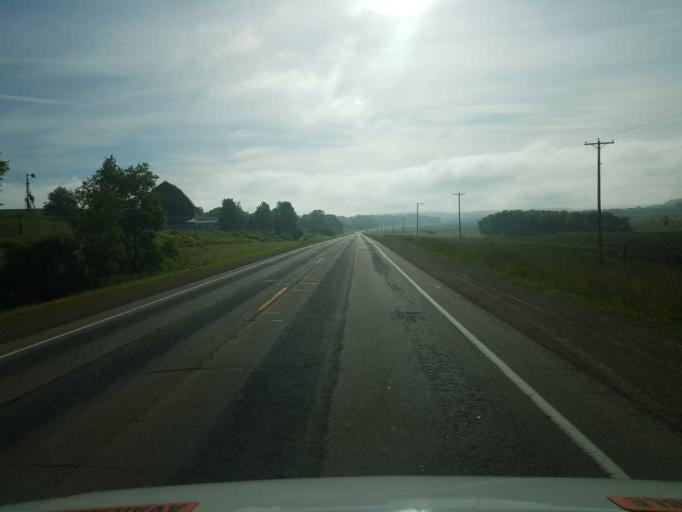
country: US
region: Wisconsin
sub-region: Vernon County
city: Hillsboro
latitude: 43.6775
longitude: -90.3058
